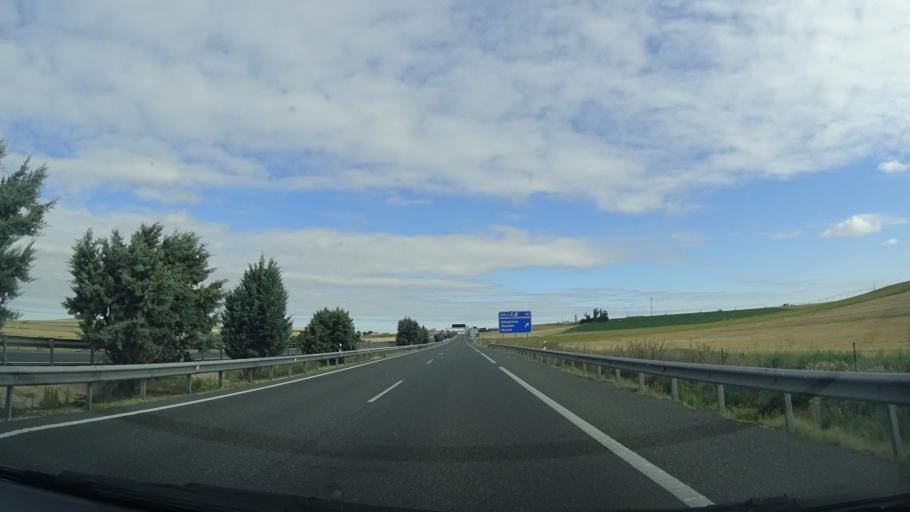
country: ES
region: Castille and Leon
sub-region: Provincia de Valladolid
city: Ataquines
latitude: 41.1688
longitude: -4.8011
